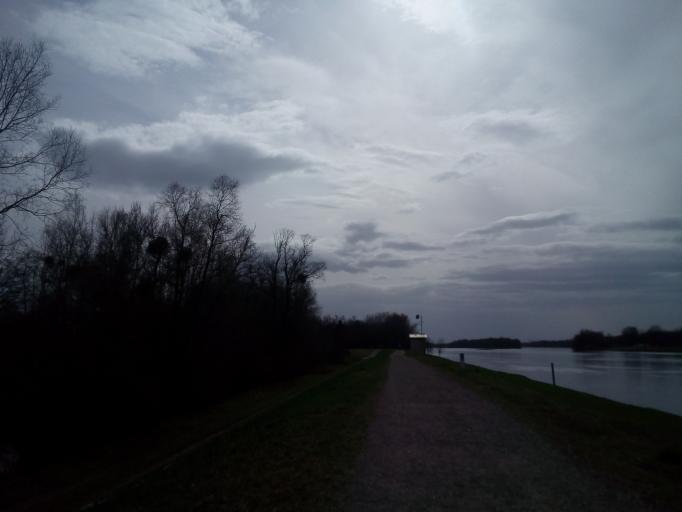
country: DE
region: Baden-Wuerttemberg
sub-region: Freiburg Region
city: Rheinau
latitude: 48.7096
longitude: 7.9511
